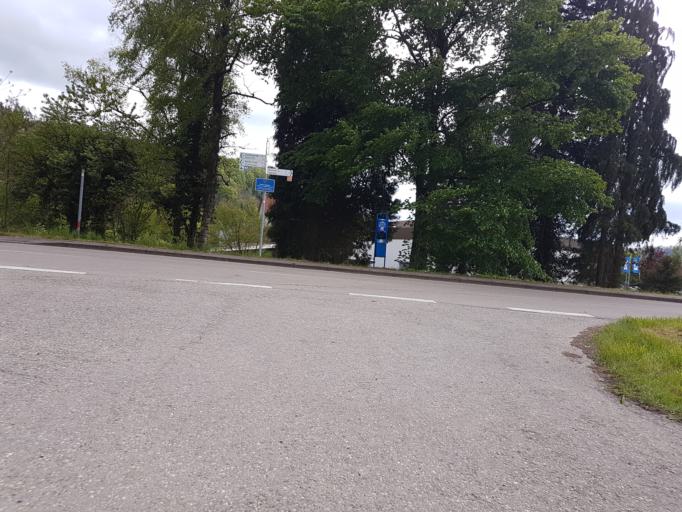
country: DE
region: Baden-Wuerttemberg
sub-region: Freiburg Region
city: Eggingen
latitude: 47.6930
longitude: 8.3988
